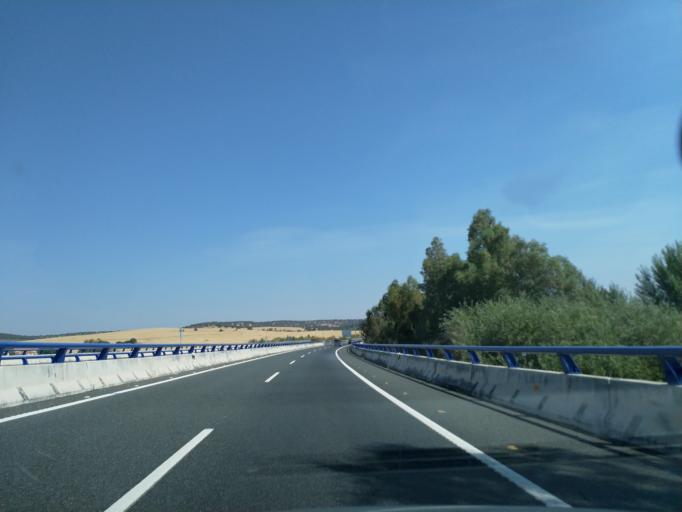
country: ES
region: Extremadura
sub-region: Provincia de Badajoz
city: Aljucen
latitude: 39.0459
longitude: -6.3382
